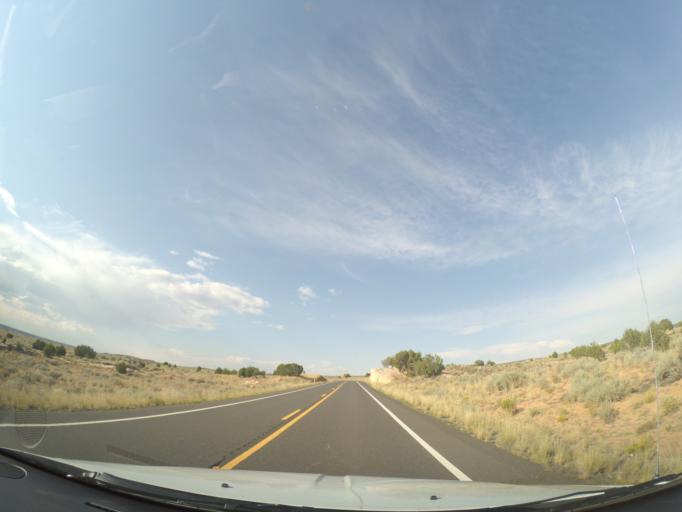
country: US
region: Arizona
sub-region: Coconino County
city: Kaibito
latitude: 36.5011
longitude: -111.4081
